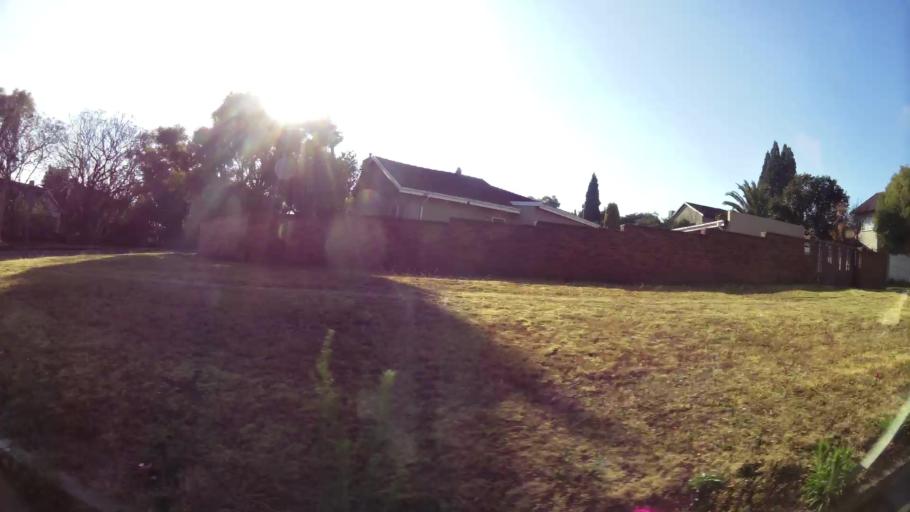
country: ZA
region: Gauteng
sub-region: City of Johannesburg Metropolitan Municipality
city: Modderfontein
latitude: -26.1359
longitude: 28.1669
